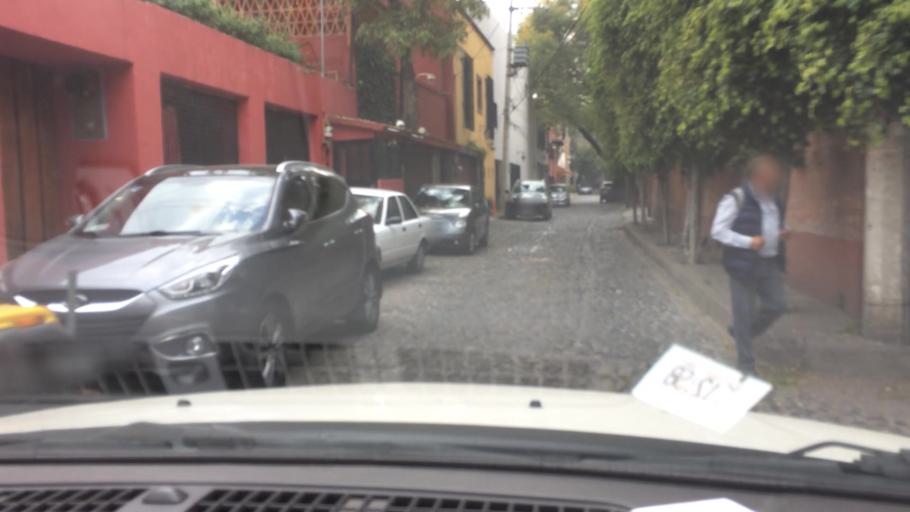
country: MX
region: Mexico City
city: Alvaro Obregon
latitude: 19.3536
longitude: -99.1958
